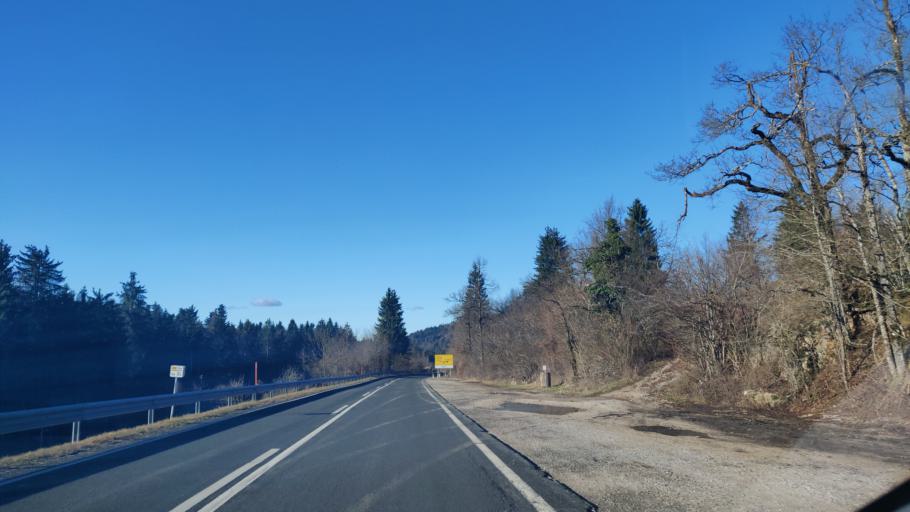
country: SI
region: Logatec
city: Logatec
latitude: 45.8915
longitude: 14.1924
